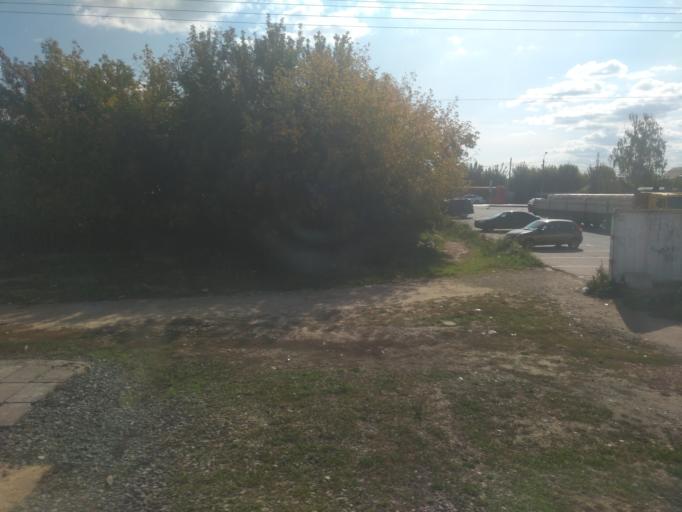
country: RU
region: Tatarstan
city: Staroye Arakchino
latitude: 55.8013
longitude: 49.0180
